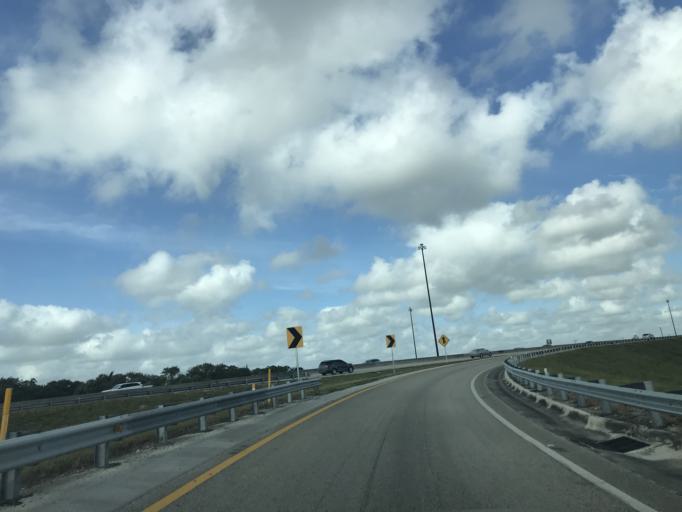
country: US
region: Florida
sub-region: Palm Beach County
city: Boca Pointe
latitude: 26.3026
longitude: -80.1687
